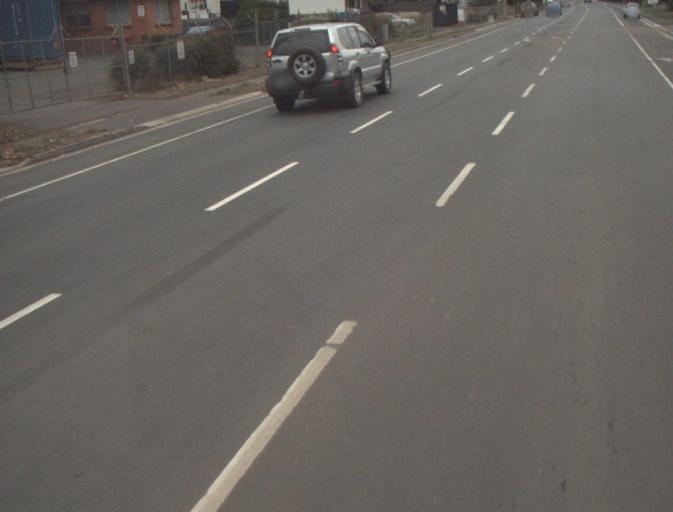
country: AU
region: Tasmania
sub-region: Launceston
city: Summerhill
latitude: -41.4881
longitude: 147.1678
